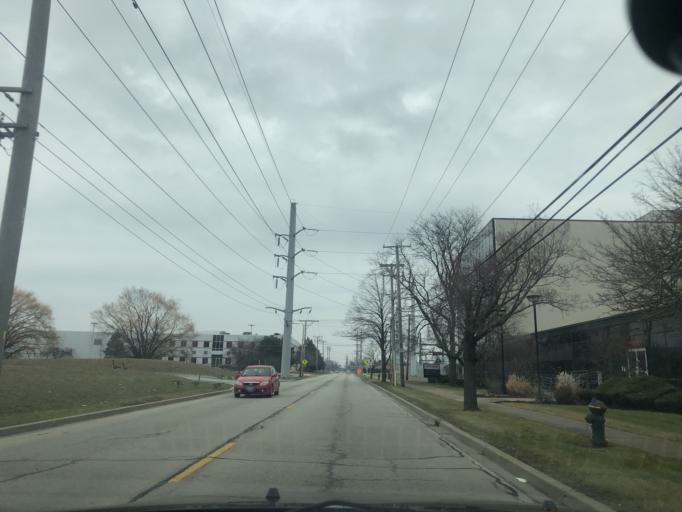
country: US
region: Illinois
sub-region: Cook County
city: Northlake
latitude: 41.9363
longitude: -87.8911
